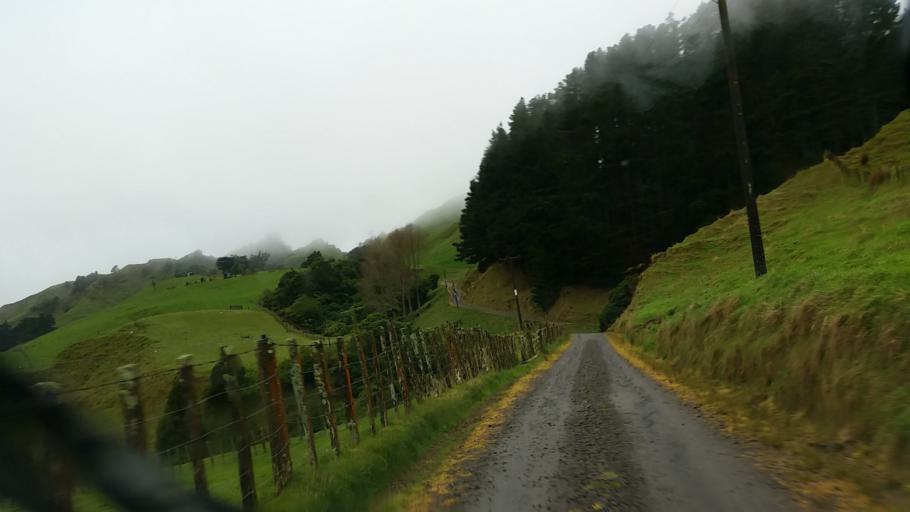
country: NZ
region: Taranaki
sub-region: South Taranaki District
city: Eltham
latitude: -39.4733
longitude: 174.4163
